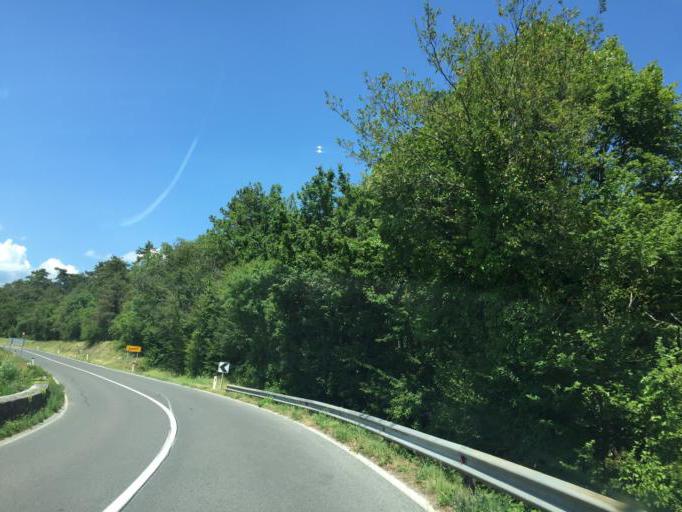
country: SI
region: Sezana
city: Sezana
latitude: 45.7273
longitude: 13.8689
